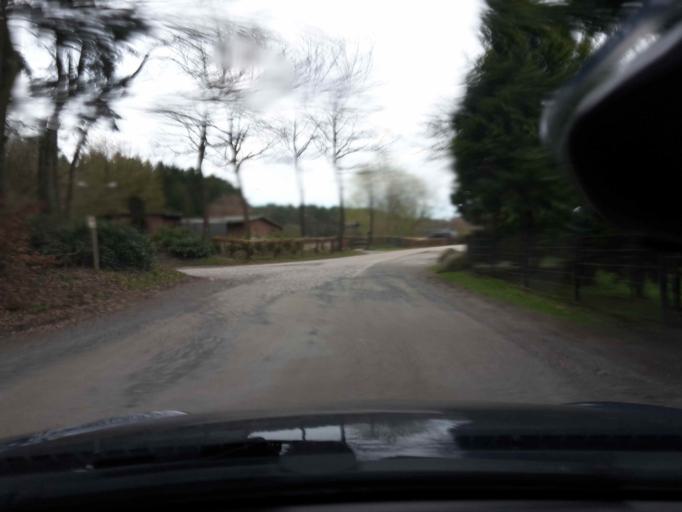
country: DE
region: Lower Saxony
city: Buchholz in der Nordheide
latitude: 53.2860
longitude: 9.8880
